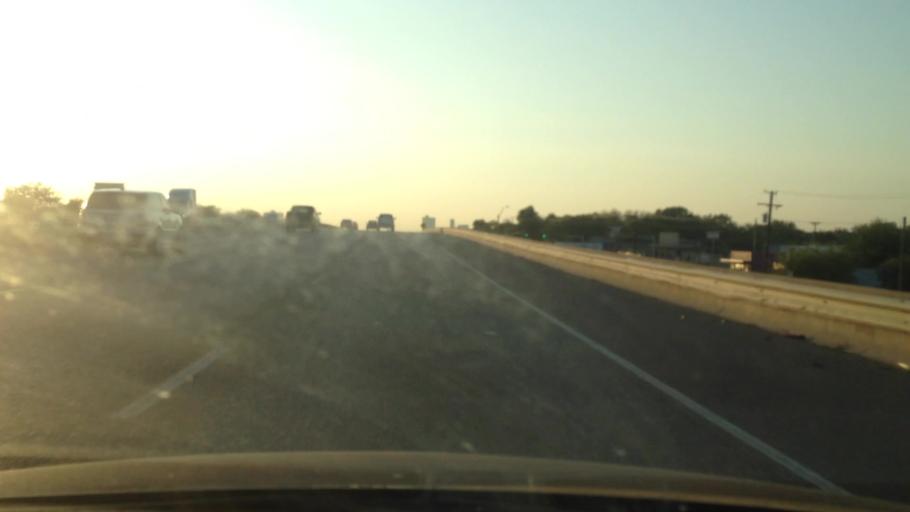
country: US
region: Texas
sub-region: Tarrant County
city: Forest Hill
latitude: 32.7134
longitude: -97.2790
